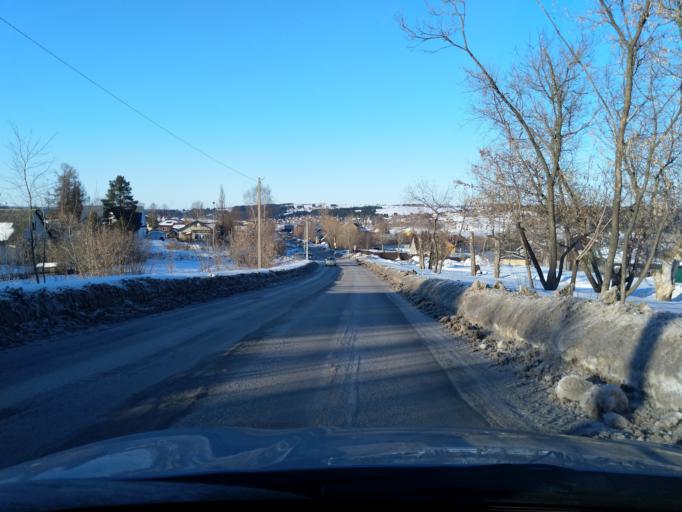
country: RU
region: Perm
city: Polazna
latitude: 58.2936
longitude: 56.4156
